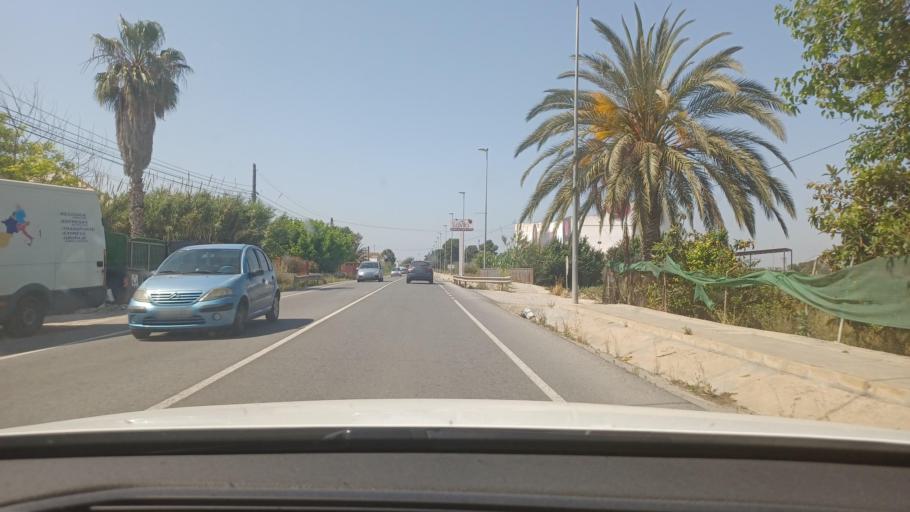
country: ES
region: Valencia
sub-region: Provincia de Alicante
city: Dolores
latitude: 38.1338
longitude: -0.7738
